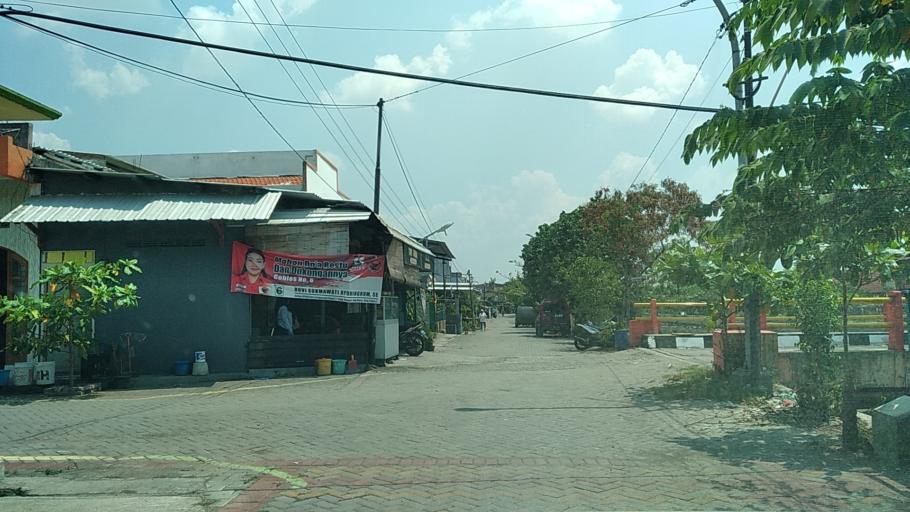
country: ID
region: Central Java
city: Semarang
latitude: -6.9624
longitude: 110.4411
